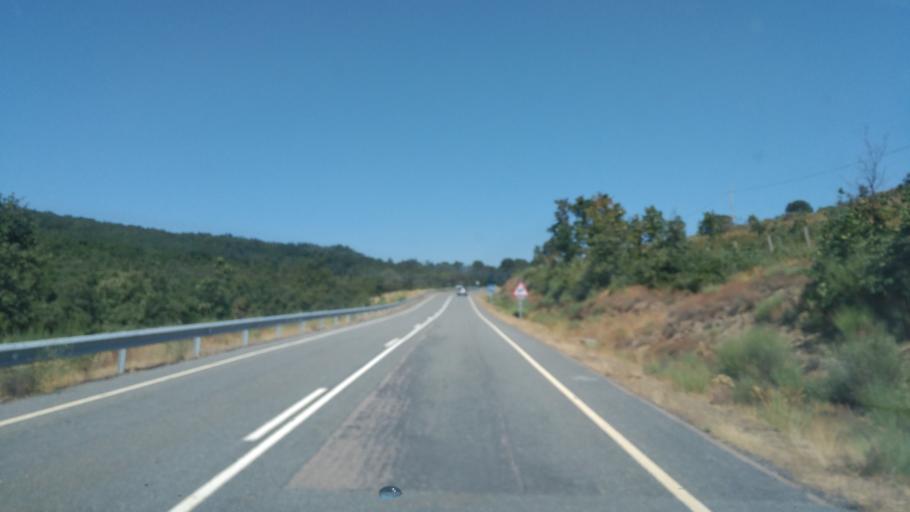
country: ES
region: Castille and Leon
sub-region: Provincia de Salamanca
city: Cereceda de la Sierra
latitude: 40.5878
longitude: -6.0881
